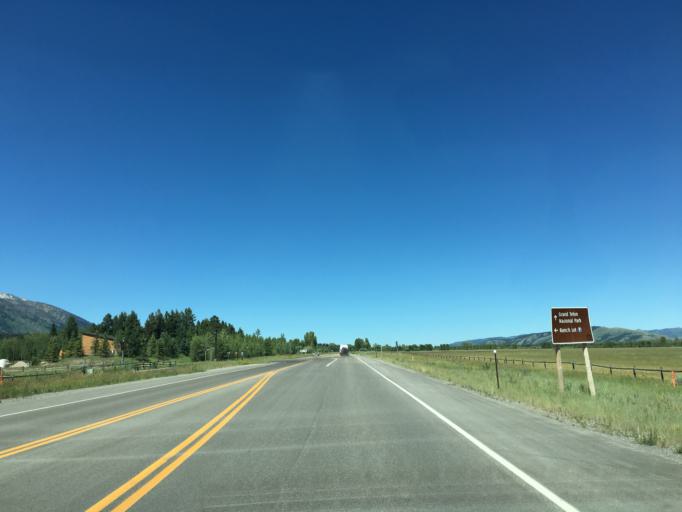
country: US
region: Wyoming
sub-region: Teton County
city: Moose Wilson Road
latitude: 43.5854
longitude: -110.8200
